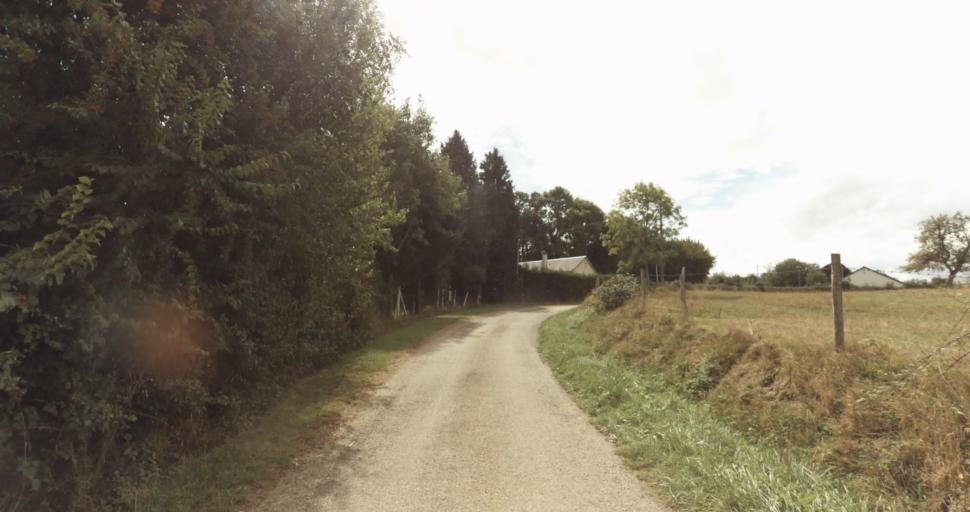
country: FR
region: Lower Normandy
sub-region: Departement du Calvados
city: Orbec
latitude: 48.9255
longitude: 0.3820
